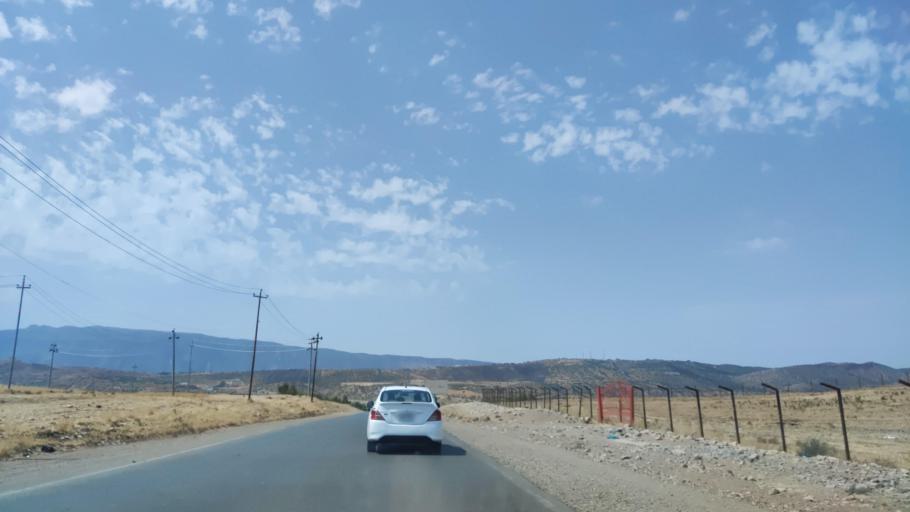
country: IQ
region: Arbil
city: Shaqlawah
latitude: 36.4611
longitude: 44.3895
